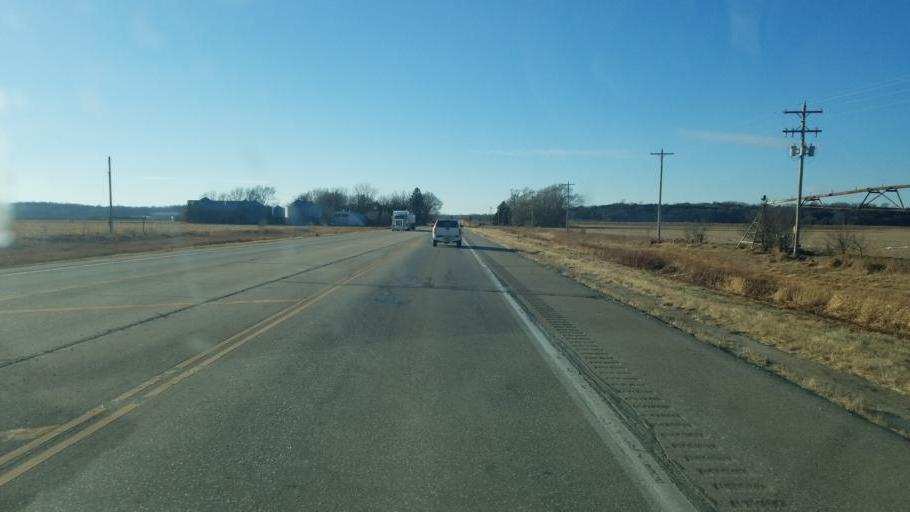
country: US
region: South Dakota
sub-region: Union County
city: Dakota Dunes
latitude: 42.4484
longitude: -96.5458
